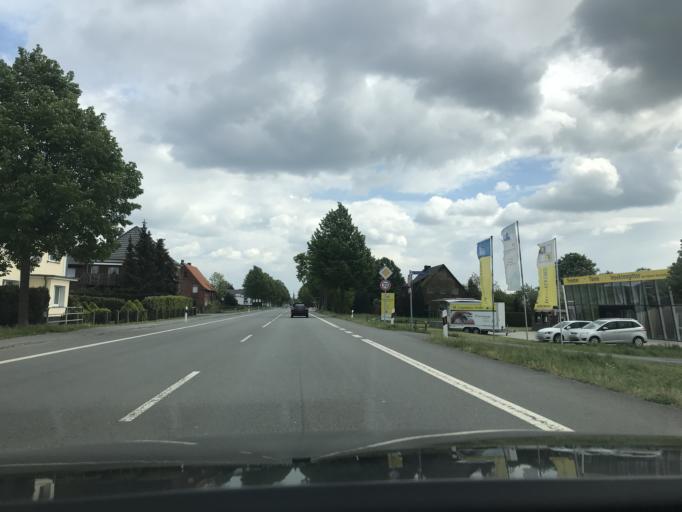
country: DE
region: North Rhine-Westphalia
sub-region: Regierungsbezirk Detmold
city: Rheda-Wiedenbruck
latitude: 51.8632
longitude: 8.2720
